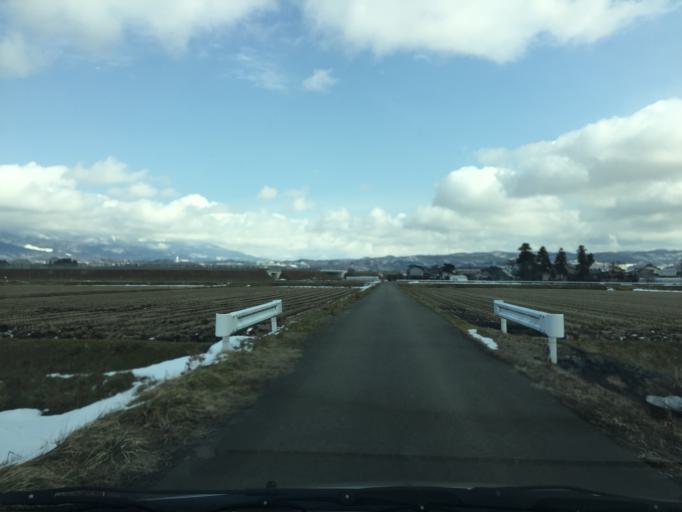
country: JP
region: Fukushima
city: Kitakata
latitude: 37.5373
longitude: 139.9048
